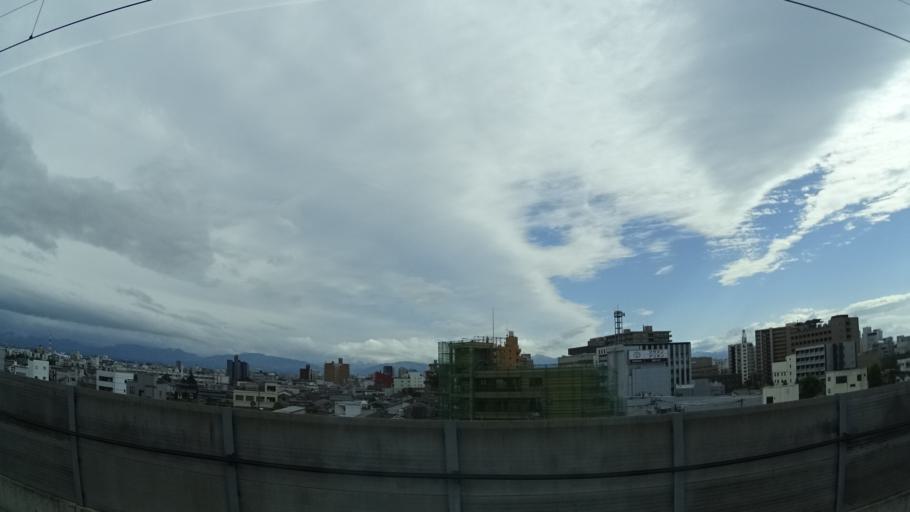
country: JP
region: Toyama
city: Toyama-shi
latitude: 36.6986
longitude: 137.2205
